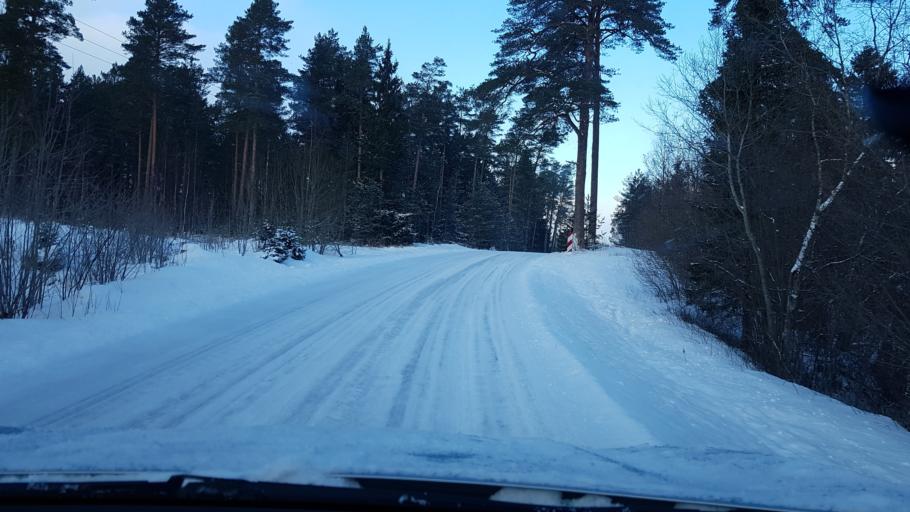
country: EE
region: Harju
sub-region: Nissi vald
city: Turba
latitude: 59.2181
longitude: 24.1400
